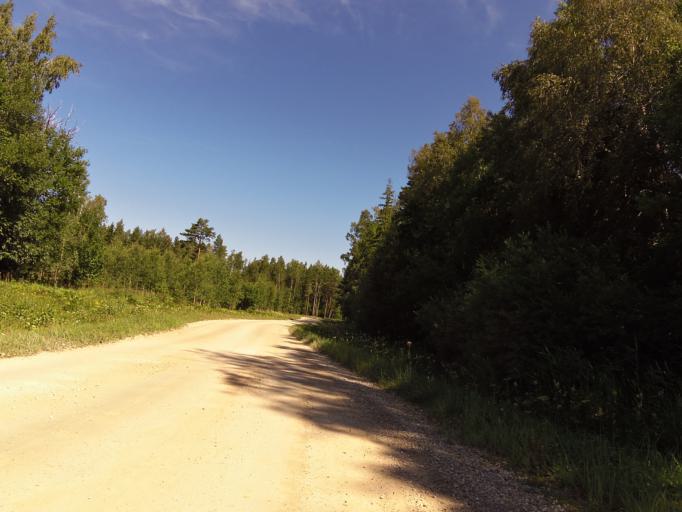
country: EE
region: Hiiumaa
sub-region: Kaerdla linn
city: Kardla
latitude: 58.9285
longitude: 22.3717
